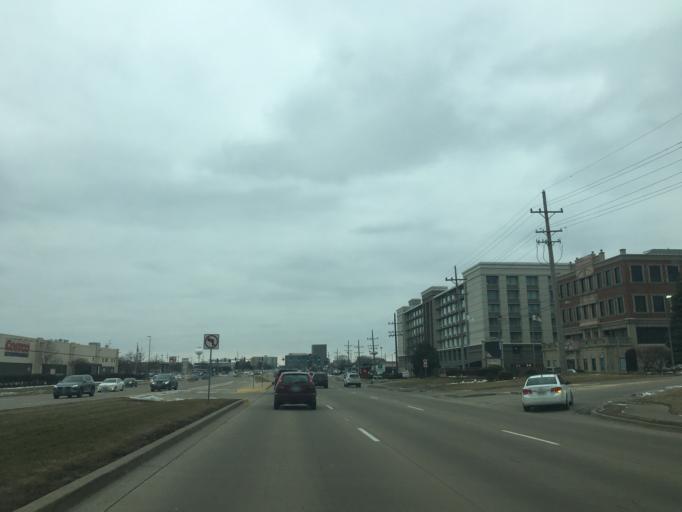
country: US
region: Illinois
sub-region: DuPage County
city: Oakbrook Terrace
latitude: 41.8465
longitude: -87.9648
